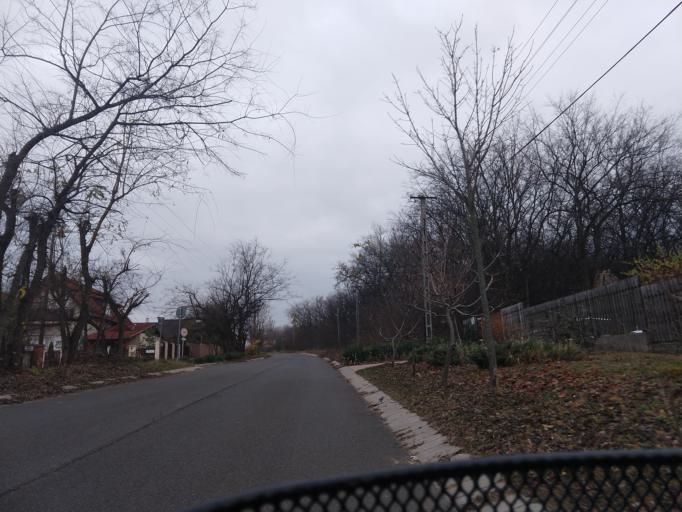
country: HU
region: Pest
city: Orbottyan
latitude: 47.6688
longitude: 19.2869
